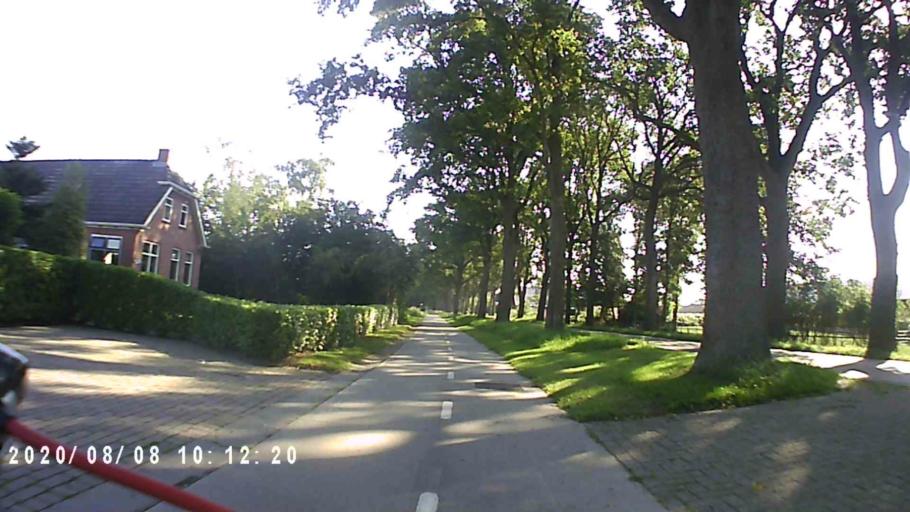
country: NL
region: Groningen
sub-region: Gemeente Leek
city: Leek
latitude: 53.1240
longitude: 6.3824
